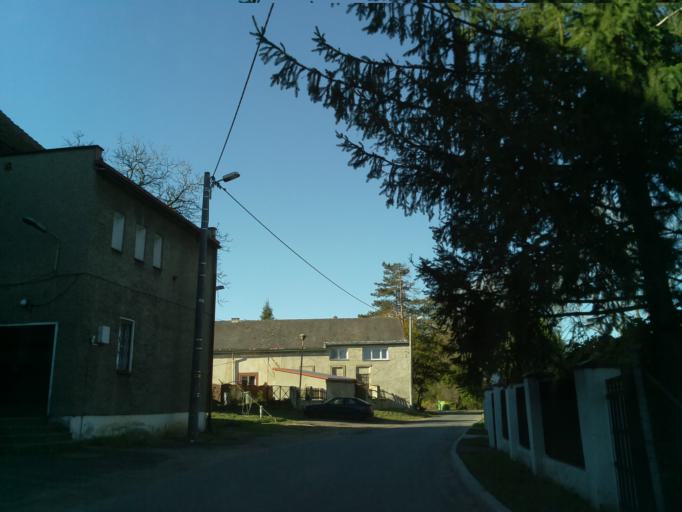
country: PL
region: Lower Silesian Voivodeship
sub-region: Powiat swidnicki
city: Swiebodzice
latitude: 50.8720
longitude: 16.3484
